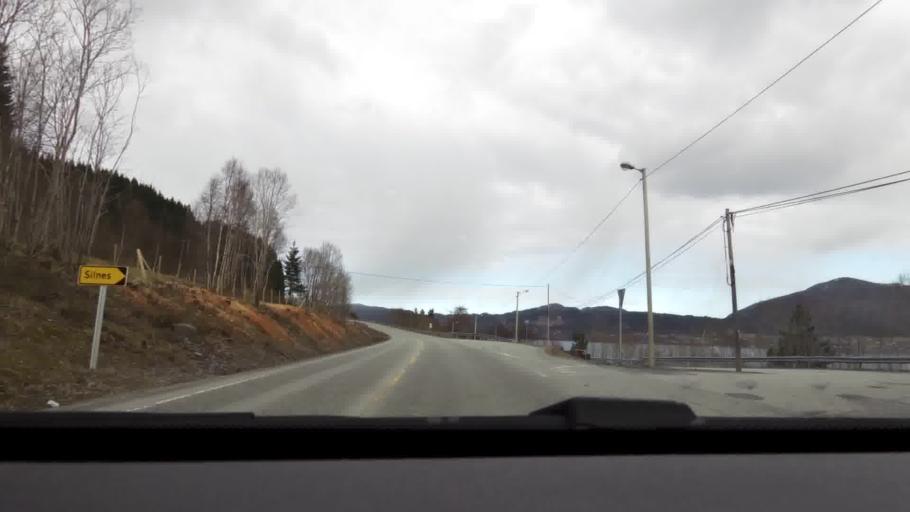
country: NO
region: More og Romsdal
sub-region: Eide
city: Eide
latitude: 62.9306
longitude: 7.4444
